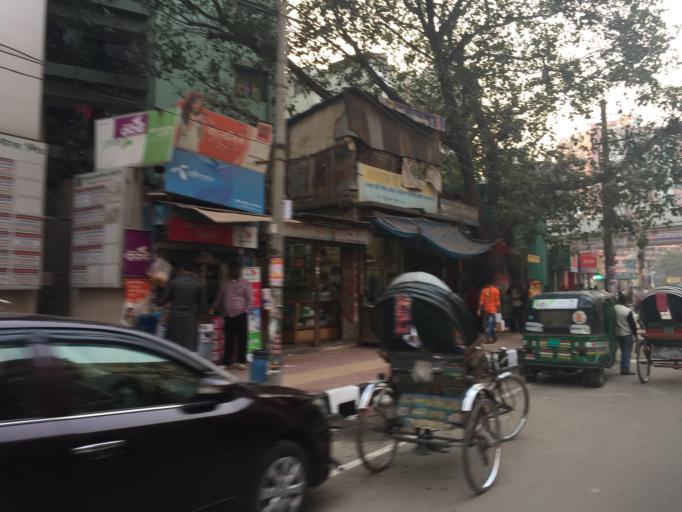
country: BD
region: Dhaka
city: Paltan
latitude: 23.7413
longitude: 90.4125
